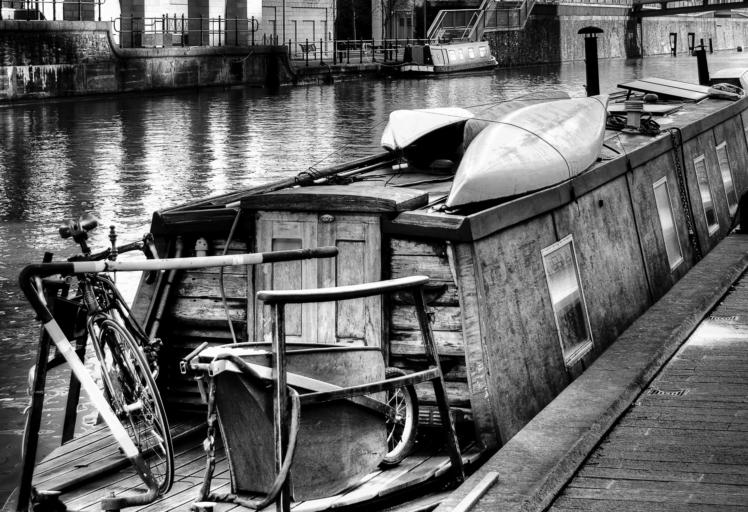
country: GB
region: England
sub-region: Bristol
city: Bristol
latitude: 51.4528
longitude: -2.5839
